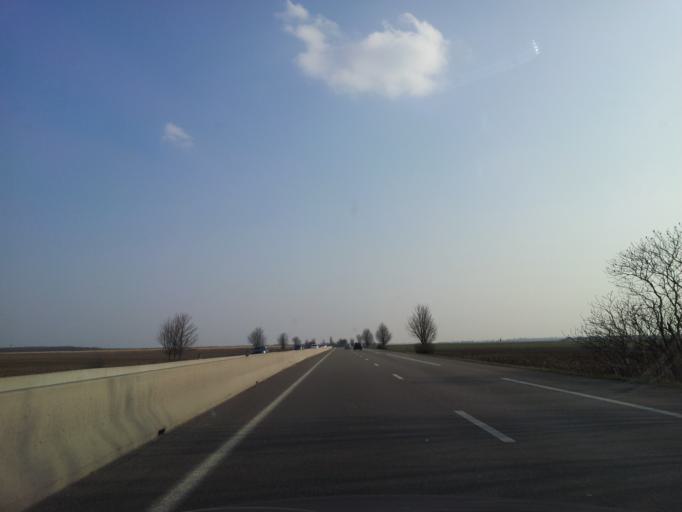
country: FR
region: Alsace
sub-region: Departement du Haut-Rhin
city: Meyenheim
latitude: 47.9078
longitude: 7.3662
